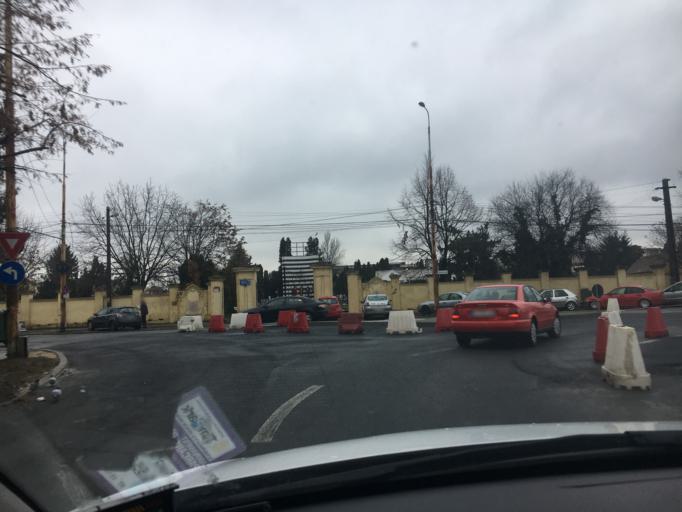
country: RO
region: Timis
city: Timisoara
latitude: 45.7678
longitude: 21.2260
